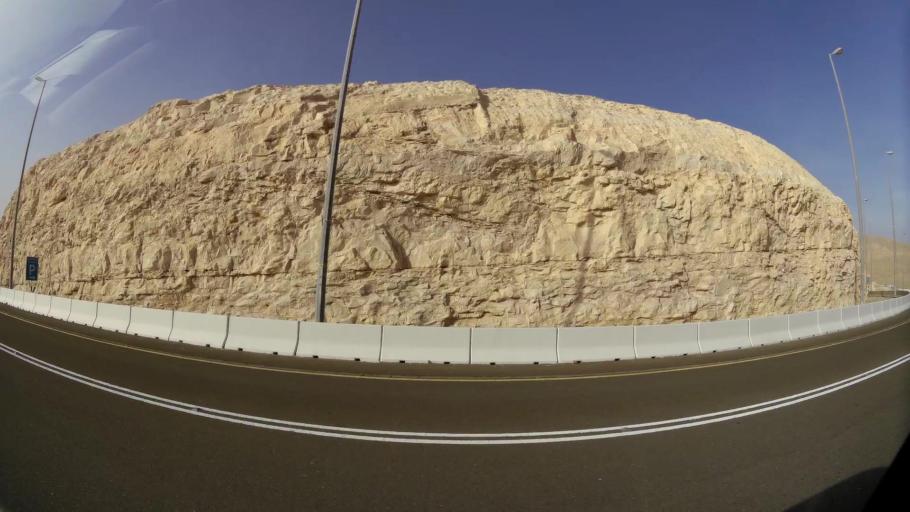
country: AE
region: Abu Dhabi
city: Al Ain
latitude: 24.1066
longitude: 55.7579
